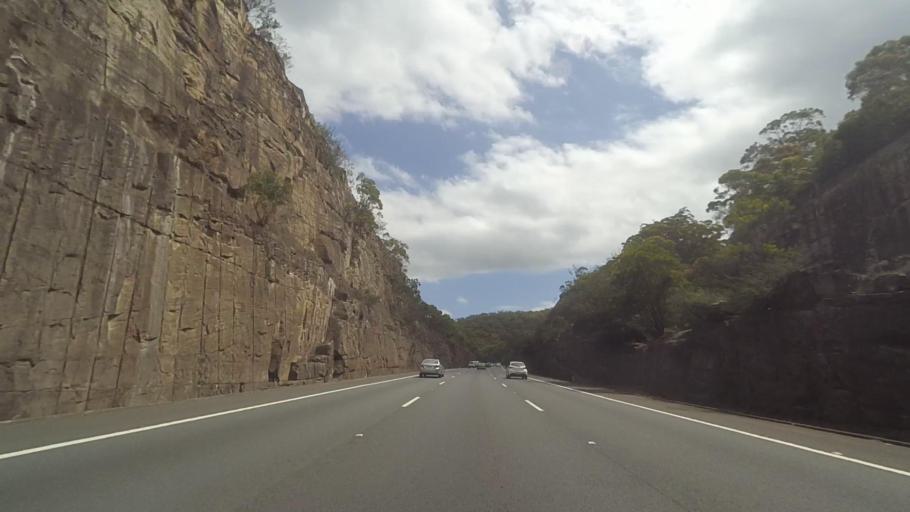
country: AU
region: New South Wales
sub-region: Hornsby Shire
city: Berowra
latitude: -33.5484
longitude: 151.1956
